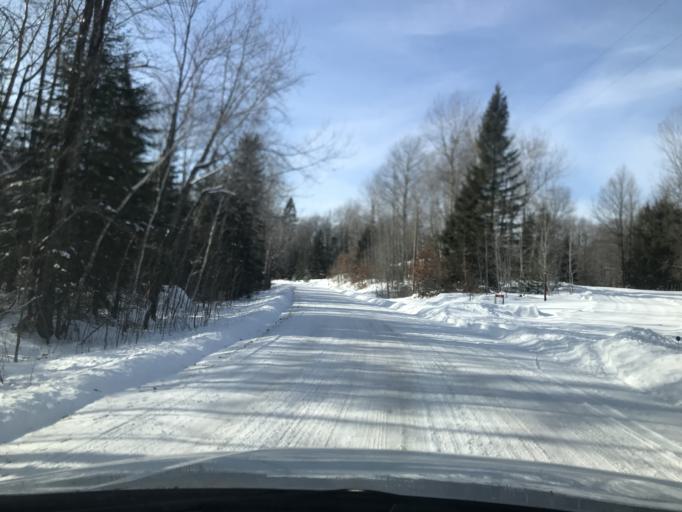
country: US
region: Wisconsin
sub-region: Oconto County
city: Gillett
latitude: 45.1486
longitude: -88.2255
